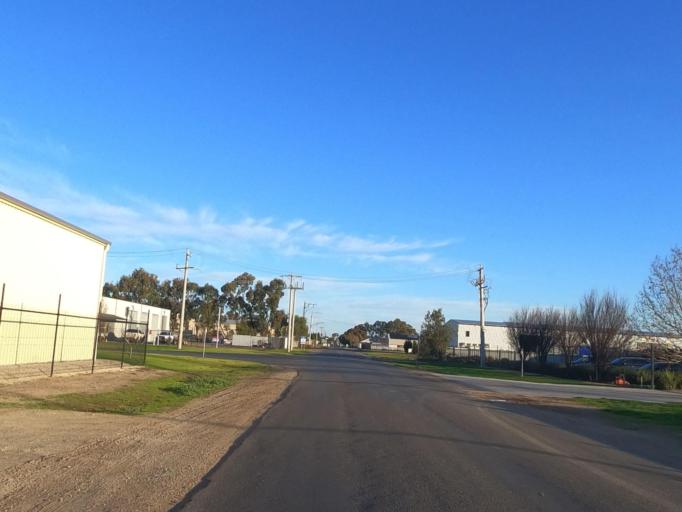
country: AU
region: Victoria
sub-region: Swan Hill
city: Swan Hill
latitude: -35.3265
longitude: 143.5352
